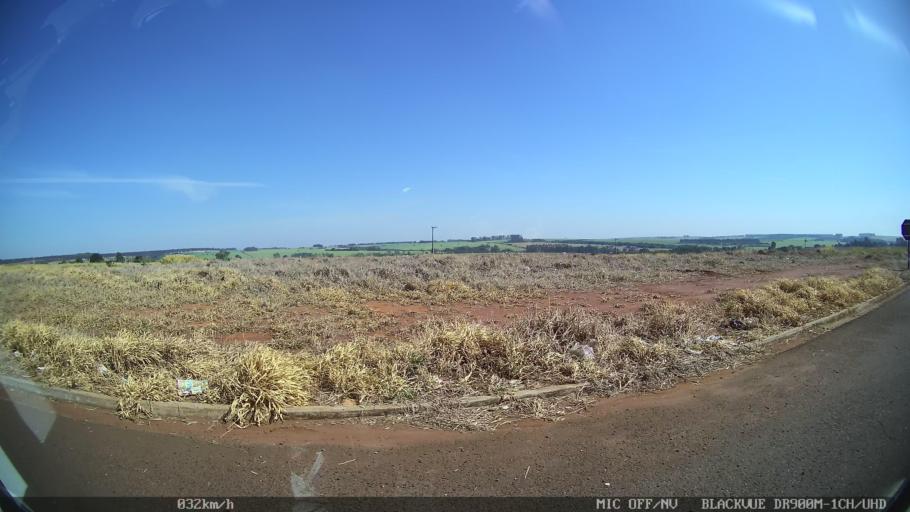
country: BR
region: Sao Paulo
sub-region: Batatais
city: Batatais
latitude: -20.8760
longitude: -47.6003
